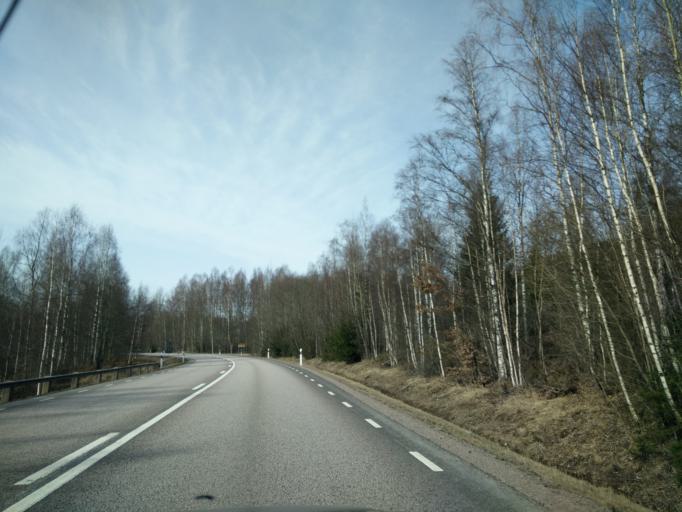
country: SE
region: Vaermland
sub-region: Hagfors Kommun
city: Hagfors
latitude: 60.0349
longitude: 13.6023
